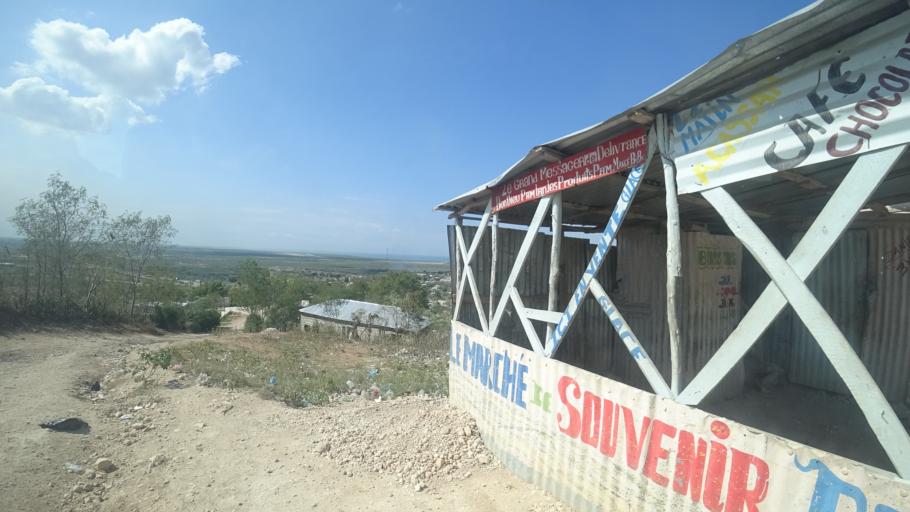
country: HT
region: Ouest
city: Croix des Bouquets
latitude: 18.6617
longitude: -72.2868
